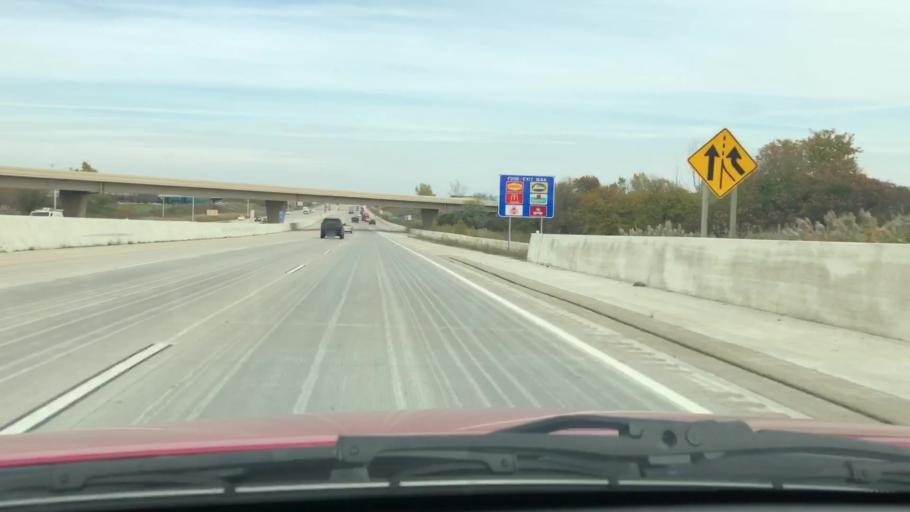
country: US
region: Wisconsin
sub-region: Brown County
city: De Pere
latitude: 44.4548
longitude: -88.0880
